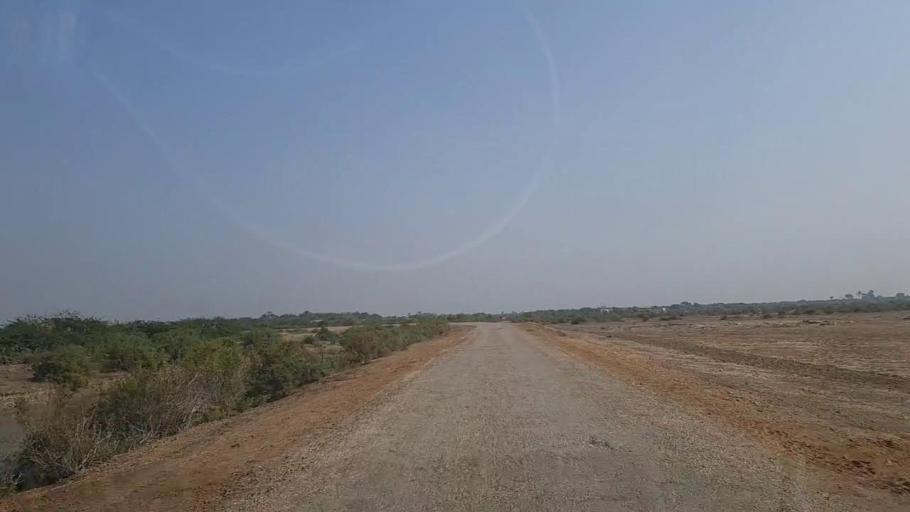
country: PK
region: Sindh
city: Keti Bandar
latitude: 24.2230
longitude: 67.6690
